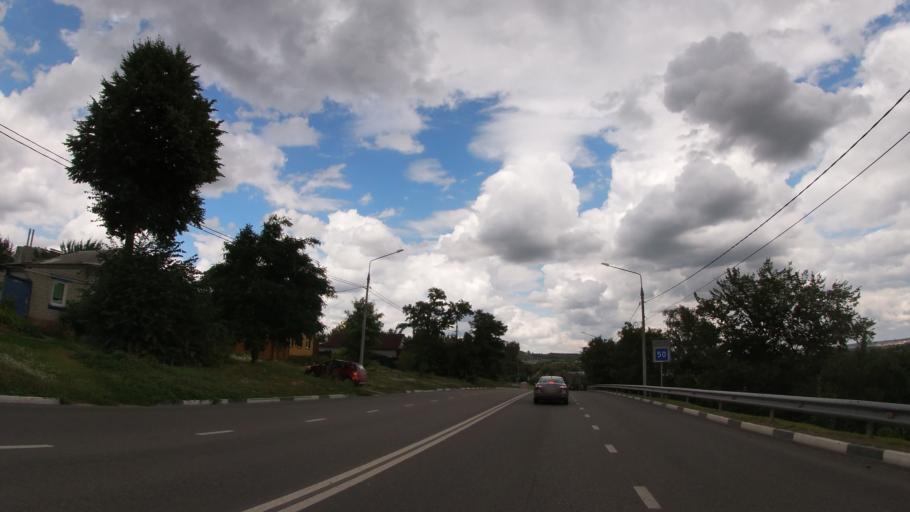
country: RU
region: Belgorod
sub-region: Belgorodskiy Rayon
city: Belgorod
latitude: 50.6038
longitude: 36.6103
